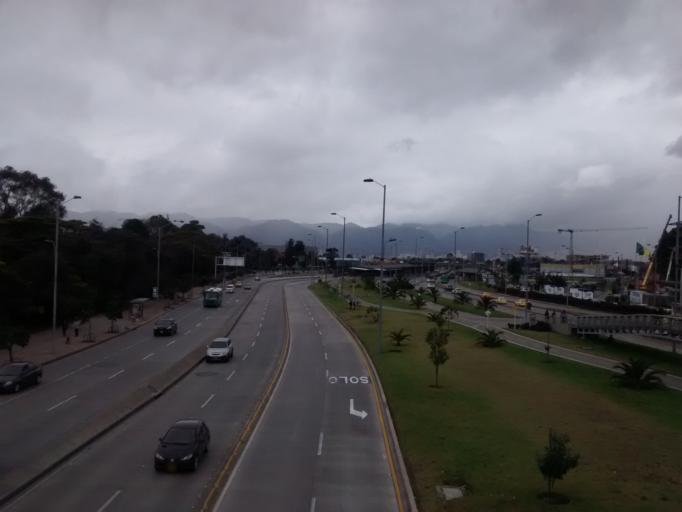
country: CO
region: Bogota D.C.
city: Bogota
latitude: 4.6846
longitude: -74.1241
